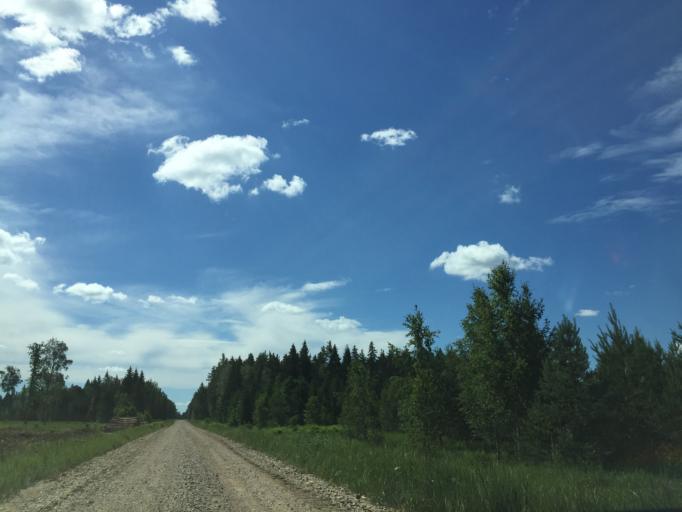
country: LV
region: Ventspils Rajons
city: Piltene
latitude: 57.2705
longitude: 21.8343
